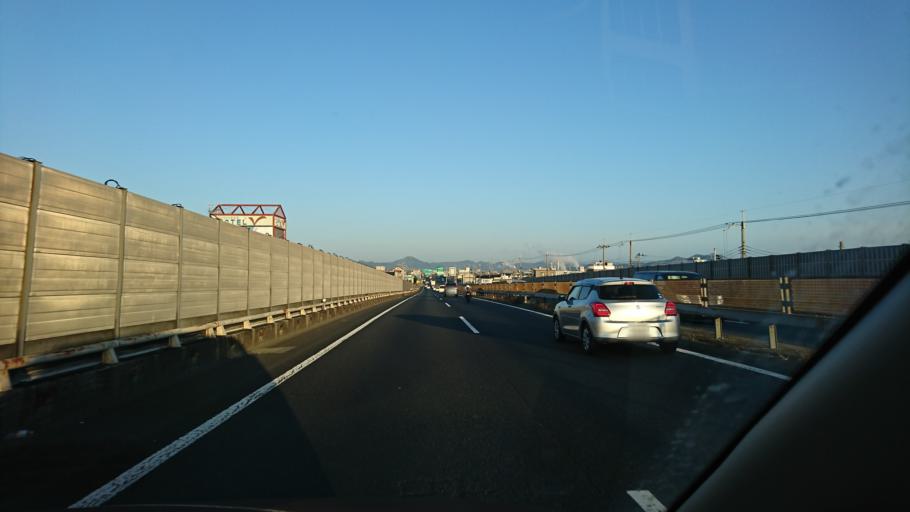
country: JP
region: Hyogo
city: Kakogawacho-honmachi
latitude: 34.7503
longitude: 134.8673
